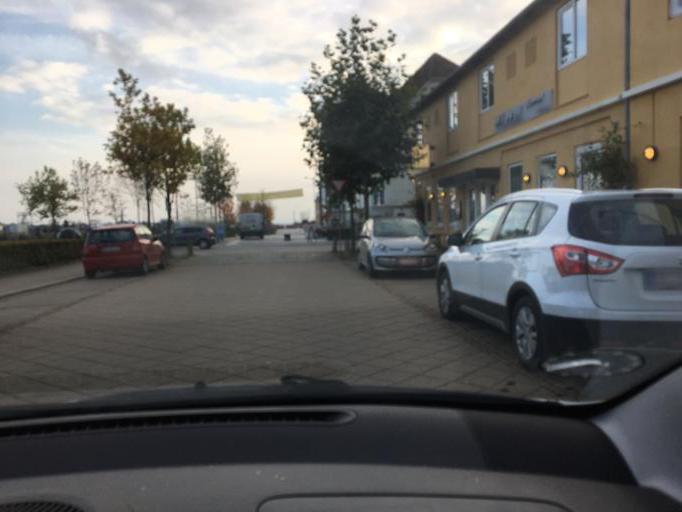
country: DK
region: South Denmark
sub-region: Fredericia Kommune
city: Fredericia
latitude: 55.5621
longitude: 9.7566
